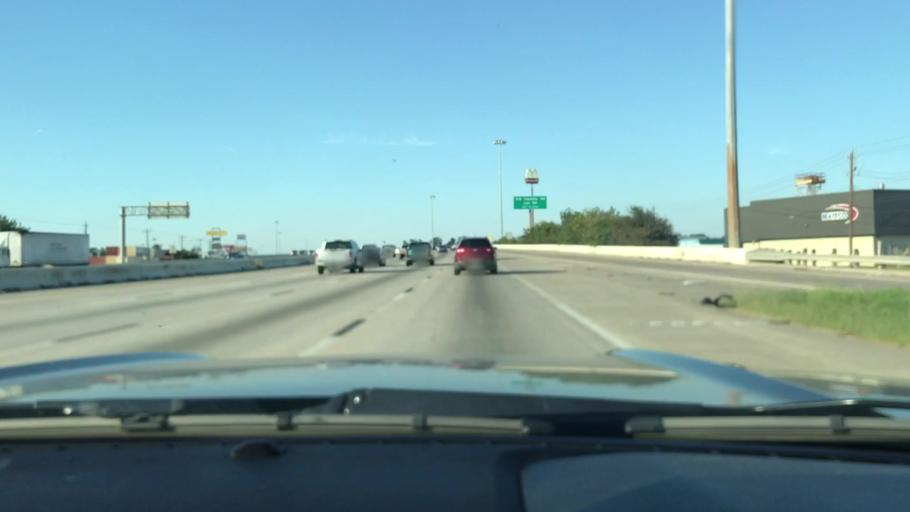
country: US
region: Texas
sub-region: Harris County
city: Aldine
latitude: 29.8987
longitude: -95.3133
